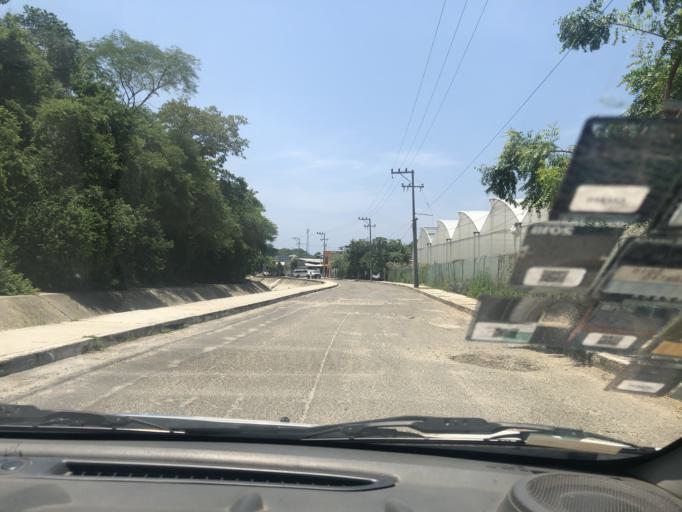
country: MX
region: Oaxaca
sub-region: Santa Maria Huatulco
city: Sector H Tres
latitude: 15.7768
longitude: -96.1488
